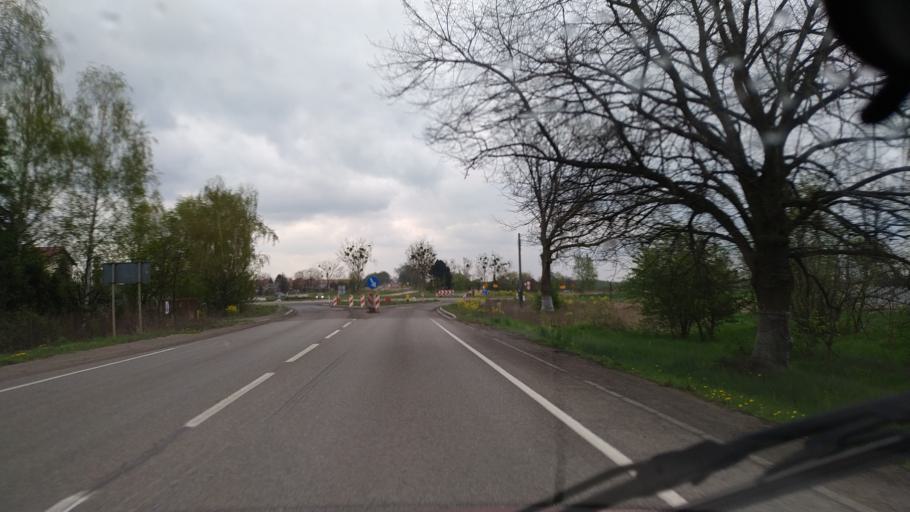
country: PL
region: Pomeranian Voivodeship
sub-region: Powiat tczewski
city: Subkowy
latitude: 54.0484
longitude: 18.7561
